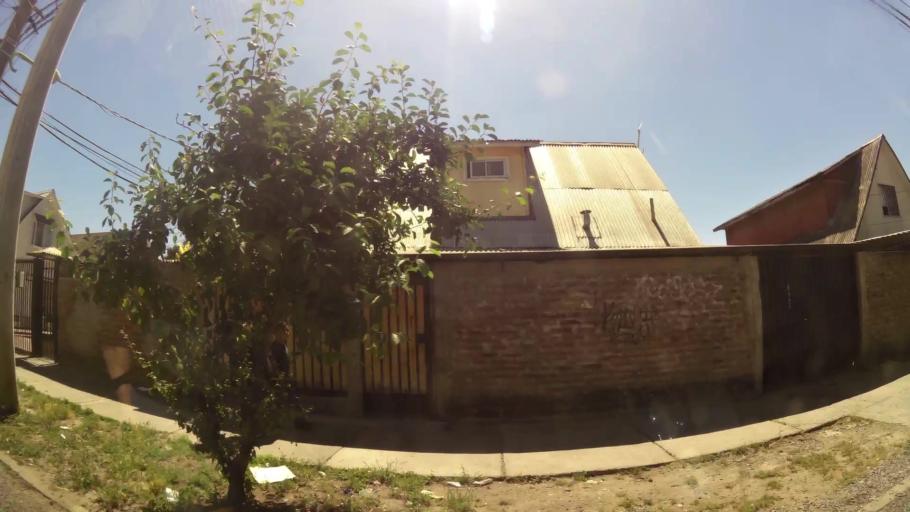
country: CL
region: Santiago Metropolitan
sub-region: Provincia de Maipo
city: San Bernardo
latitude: -33.5769
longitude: -70.6863
